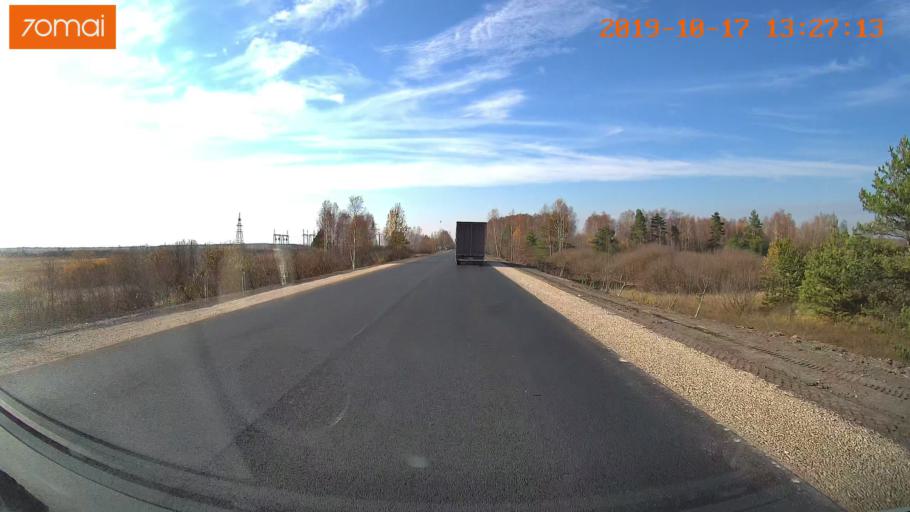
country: RU
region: Vladimir
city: Velikodvorskiy
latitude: 55.1126
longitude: 40.9005
